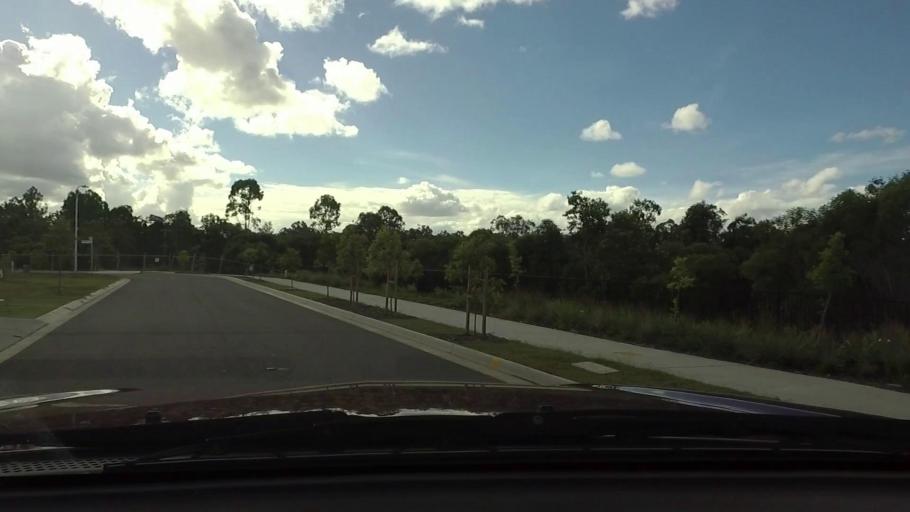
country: AU
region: Queensland
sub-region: Logan
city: Chambers Flat
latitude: -27.8046
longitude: 153.1243
